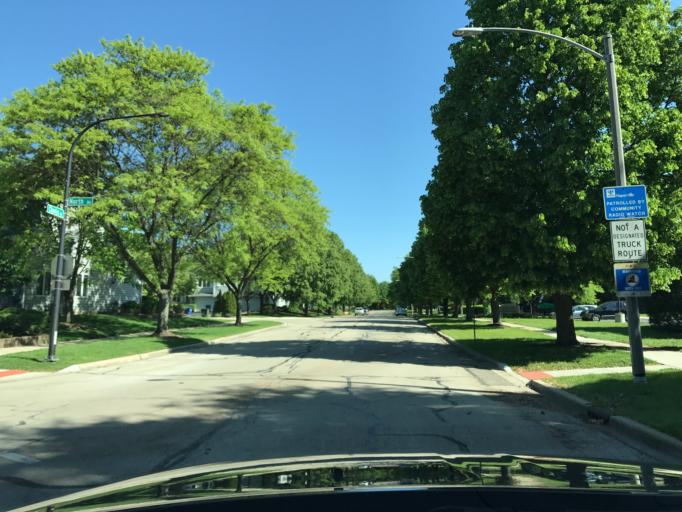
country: US
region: Illinois
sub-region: DuPage County
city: Naperville
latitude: 41.7780
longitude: -88.1296
